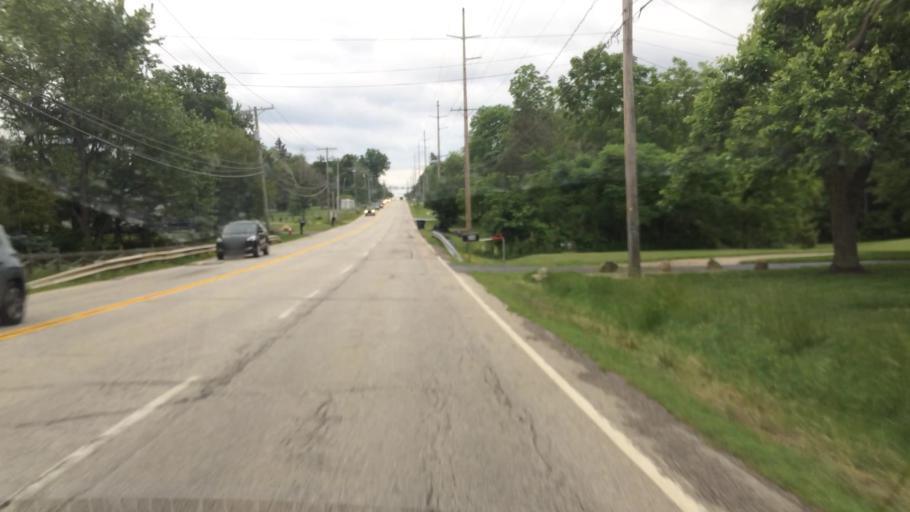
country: US
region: Ohio
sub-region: Summit County
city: Cuyahoga Falls
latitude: 41.1809
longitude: -81.5198
